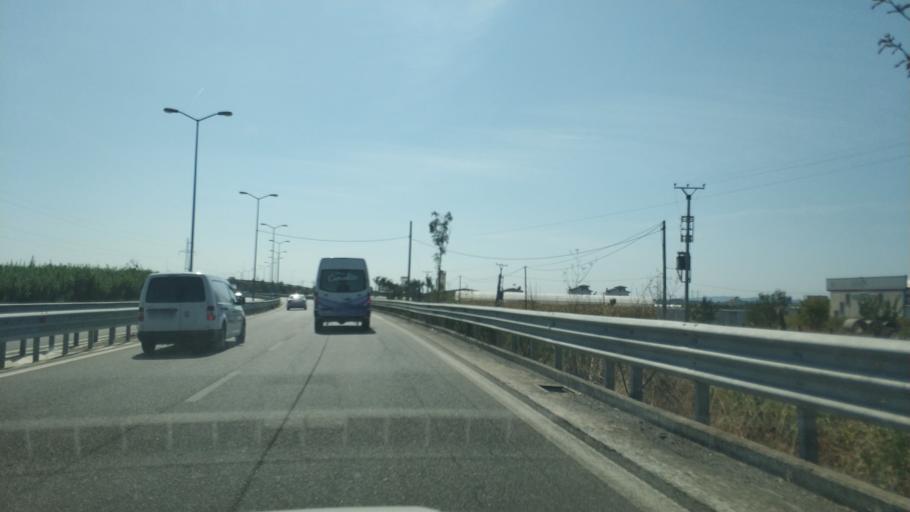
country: AL
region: Tirane
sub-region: Rrethi i Kavajes
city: Gose e Madhe
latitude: 41.0922
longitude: 19.6087
